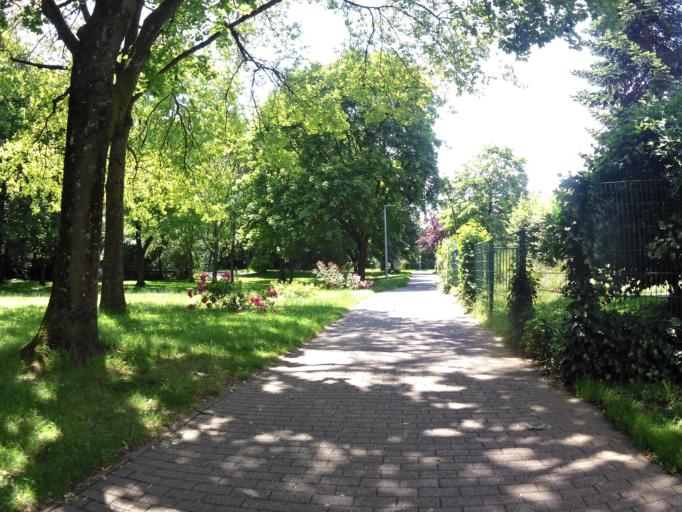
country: DE
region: Baden-Wuerttemberg
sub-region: Freiburg Region
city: Lahr
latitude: 48.3398
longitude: 7.8814
